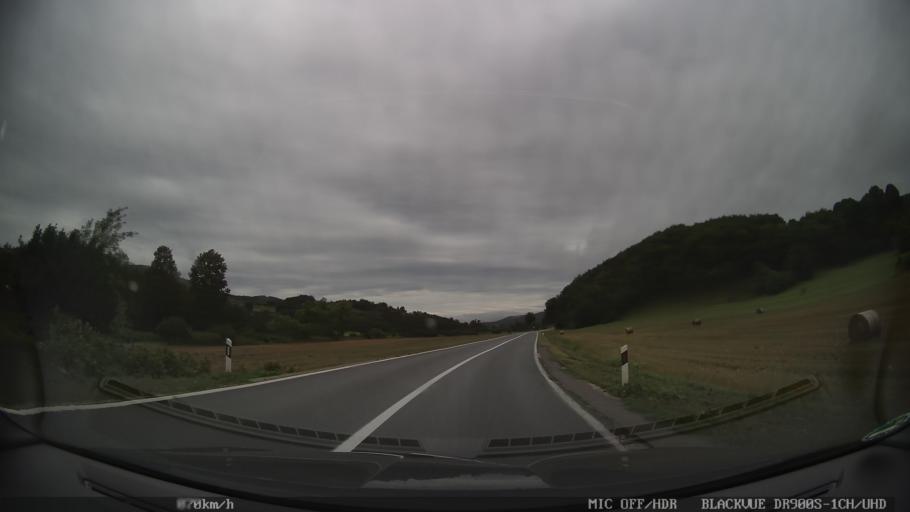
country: HR
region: Licko-Senjska
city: Brinje
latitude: 44.9323
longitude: 15.1326
